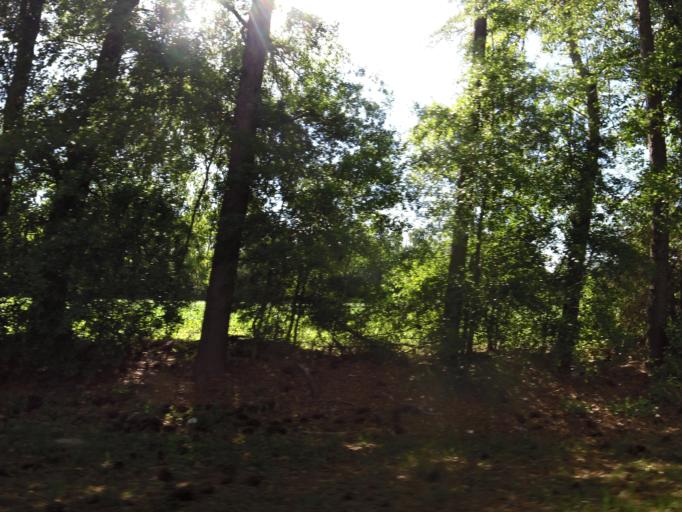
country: US
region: South Carolina
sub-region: Allendale County
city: Allendale
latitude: 33.0933
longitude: -81.2073
